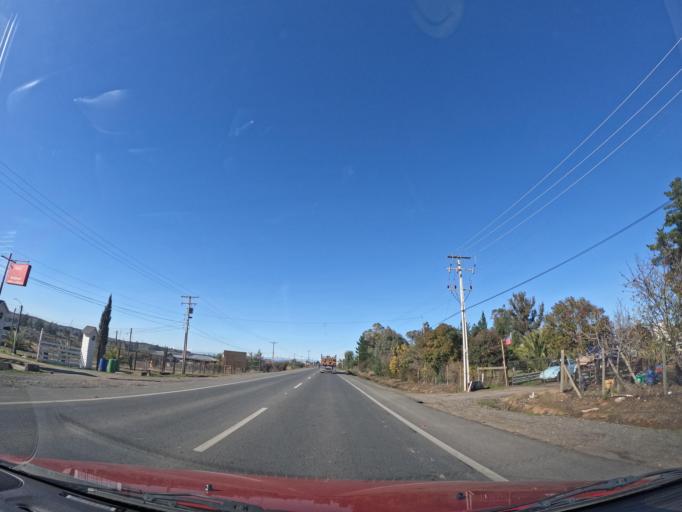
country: CL
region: Maule
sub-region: Provincia de Cauquenes
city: Cauquenes
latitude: -35.9591
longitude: -72.2668
